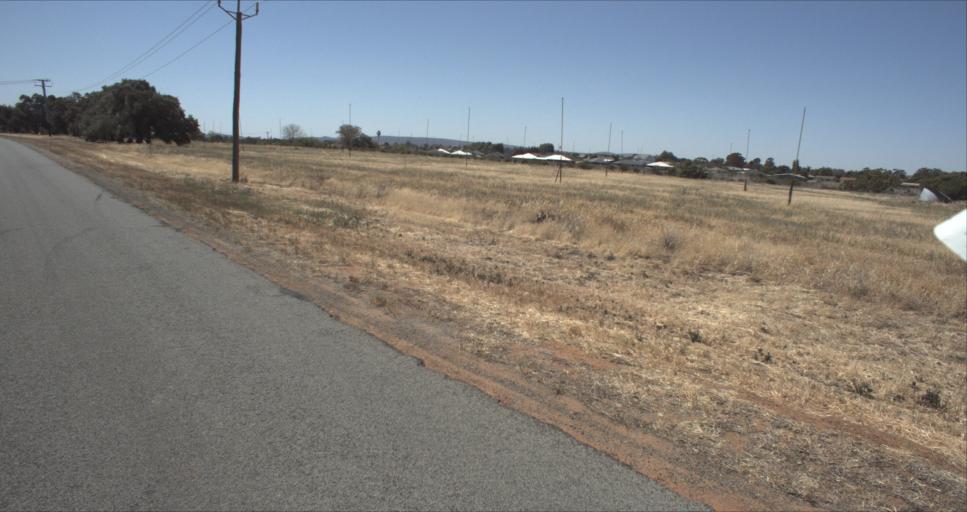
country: AU
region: New South Wales
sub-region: Leeton
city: Leeton
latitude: -34.5410
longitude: 146.3951
